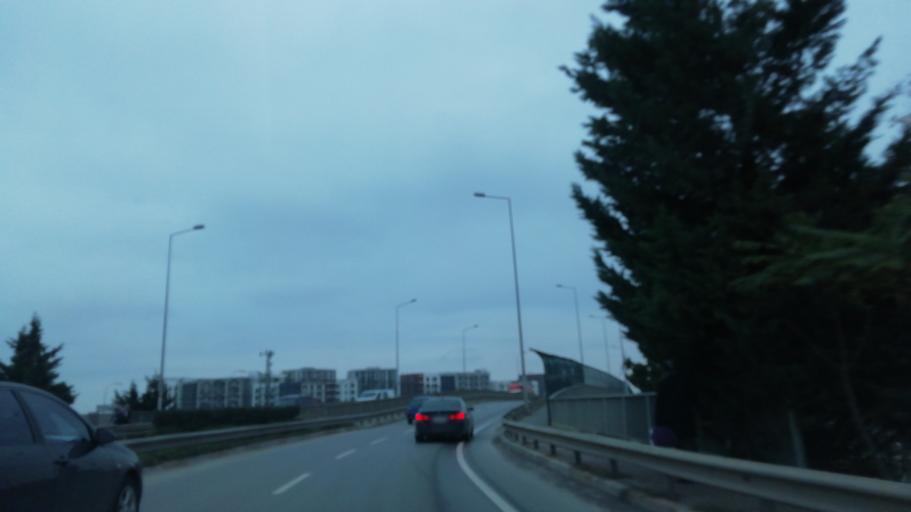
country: TR
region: Istanbul
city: Samandira
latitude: 40.9751
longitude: 29.2395
